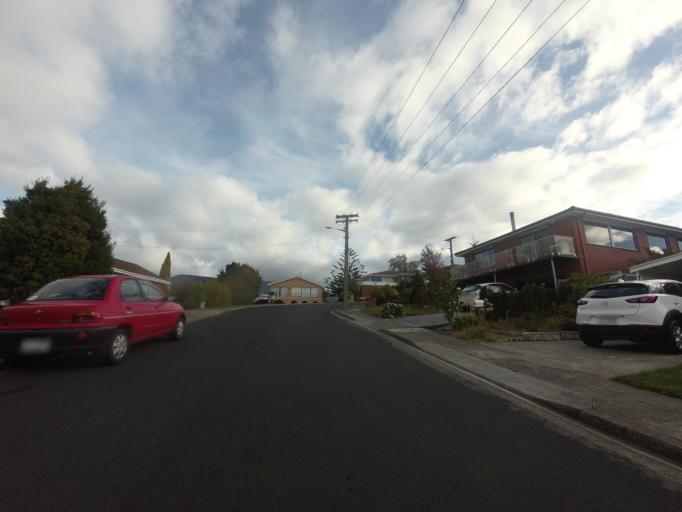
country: AU
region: Tasmania
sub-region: Glenorchy
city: Glenorchy
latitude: -42.8306
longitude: 147.2601
